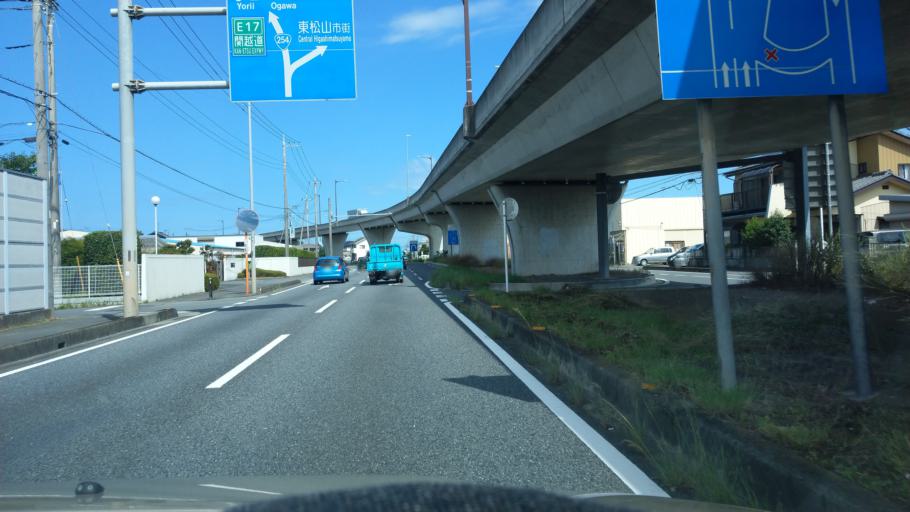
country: JP
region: Saitama
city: Sakado
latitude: 36.0214
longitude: 139.4221
